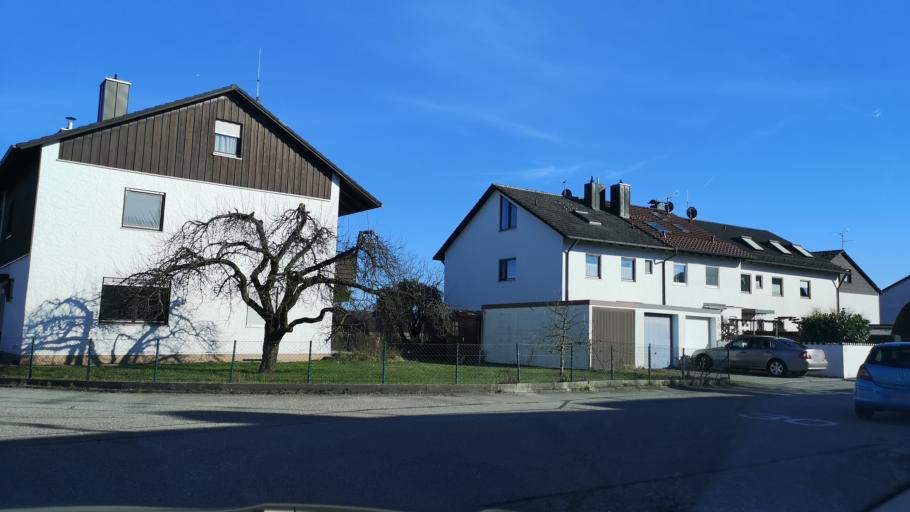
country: DE
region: Bavaria
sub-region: Upper Bavaria
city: Anzing
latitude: 48.1512
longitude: 11.8570
